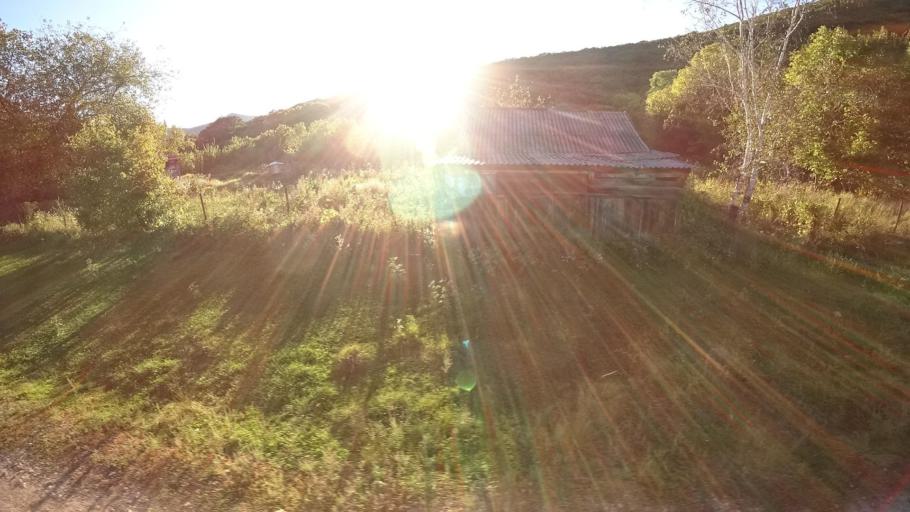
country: RU
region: Primorskiy
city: Kirovskiy
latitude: 44.8341
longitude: 133.5732
